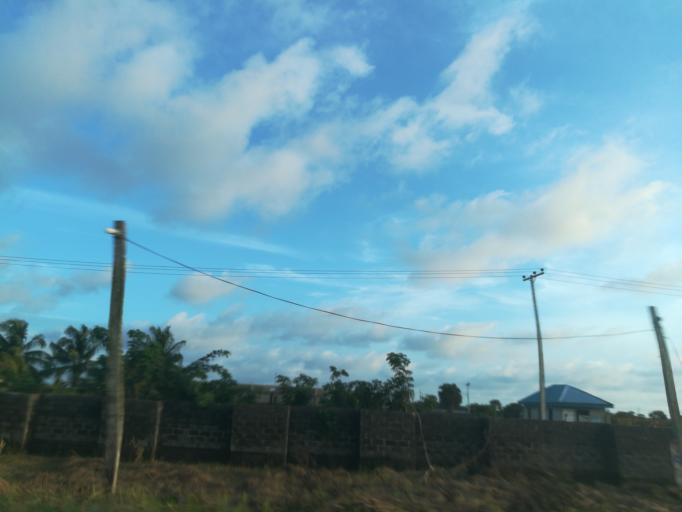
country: NG
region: Lagos
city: Badagry
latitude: 6.4713
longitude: 2.9948
